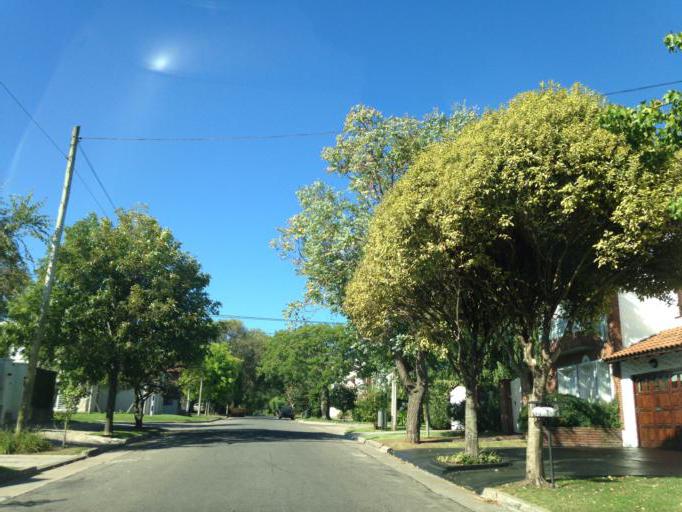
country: AR
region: Buenos Aires
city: Mar del Plata
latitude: -38.0306
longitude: -57.5466
